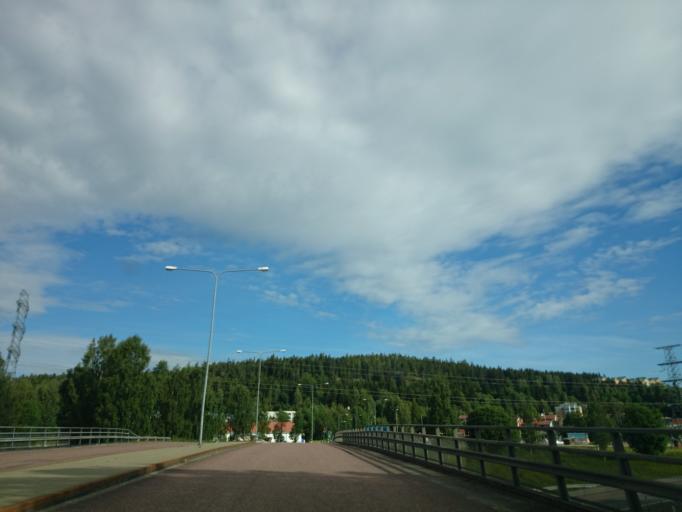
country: SE
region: Vaesternorrland
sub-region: Timra Kommun
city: Timra
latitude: 62.4800
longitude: 17.3149
